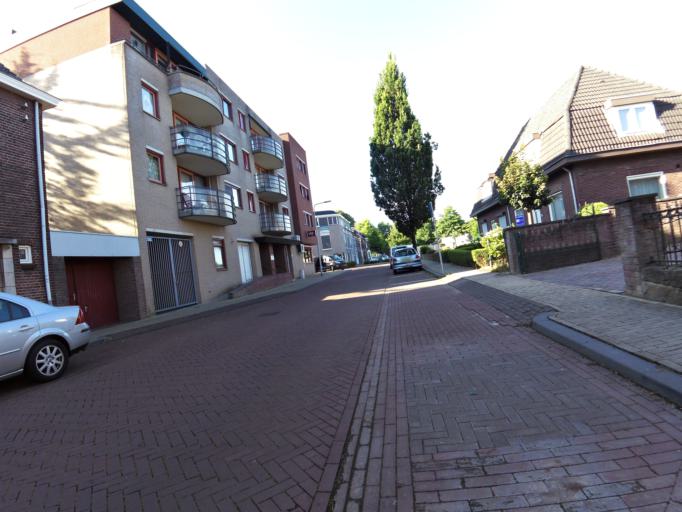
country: NL
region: Limburg
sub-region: Gemeente Kerkrade
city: Kerkrade
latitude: 50.8682
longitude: 6.0251
